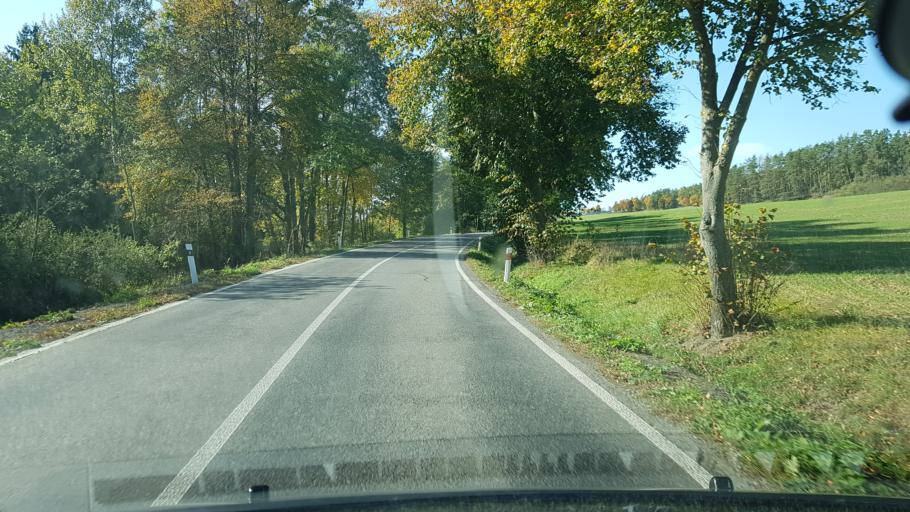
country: CZ
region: Jihocesky
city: Radomysl
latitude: 49.2982
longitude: 14.0056
